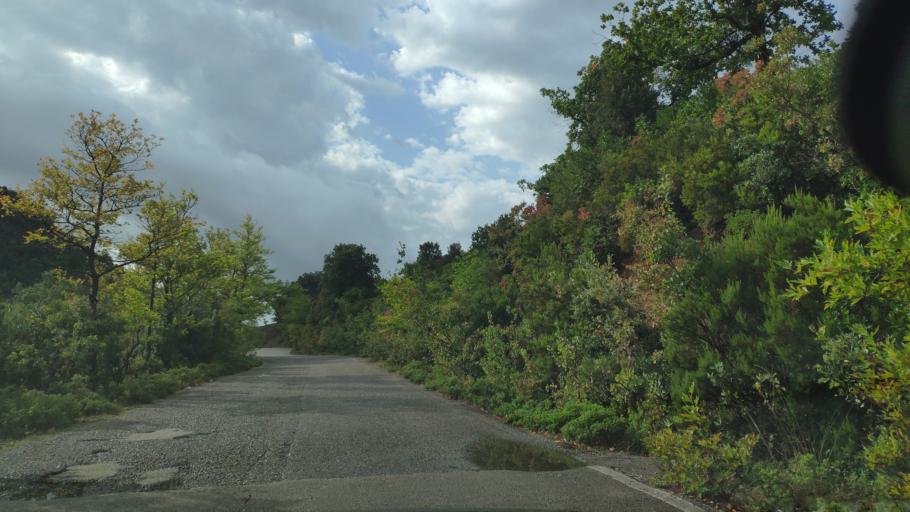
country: GR
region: West Greece
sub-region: Nomos Aitolias kai Akarnanias
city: Sardinia
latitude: 38.8565
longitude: 21.3064
